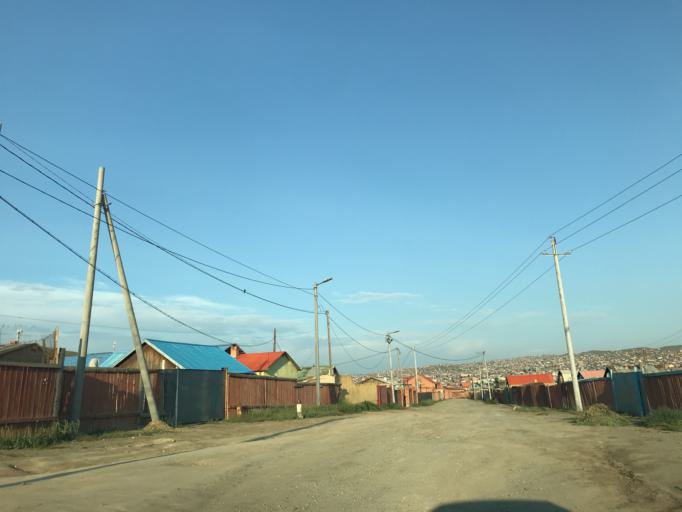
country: MN
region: Ulaanbaatar
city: Ulaanbaatar
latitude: 47.9517
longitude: 106.9391
